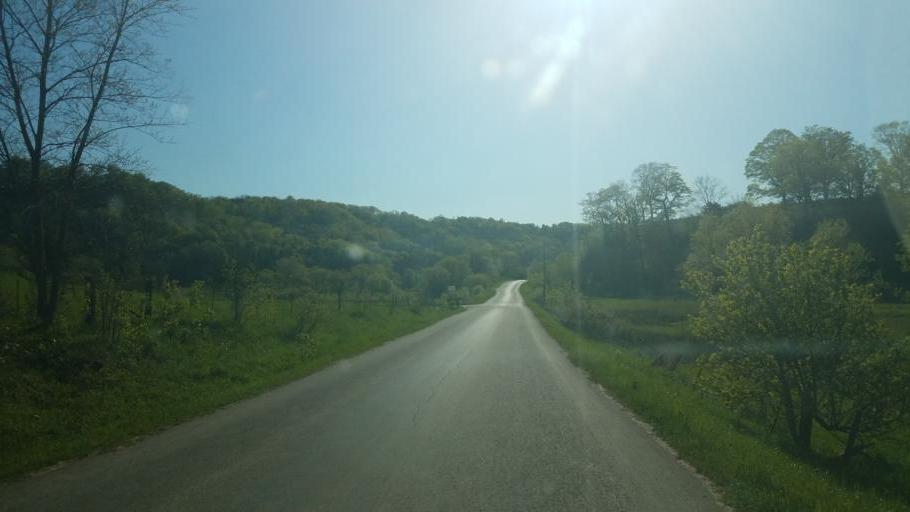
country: US
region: Wisconsin
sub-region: Vernon County
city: Hillsboro
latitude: 43.6241
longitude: -90.4831
